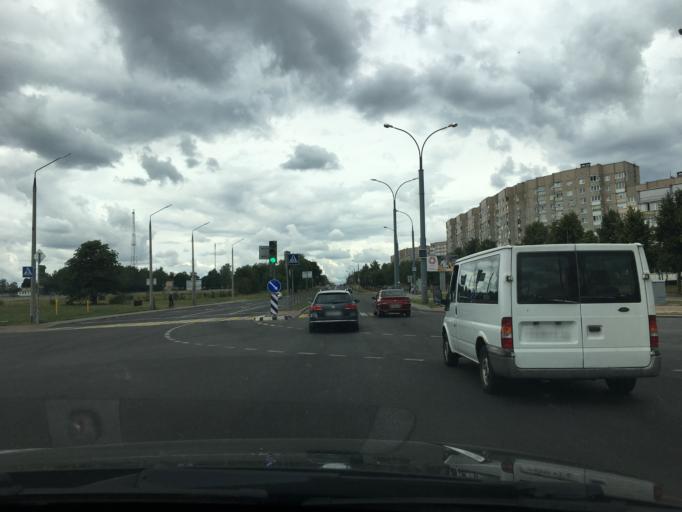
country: BY
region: Grodnenskaya
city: Hrodna
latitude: 53.6408
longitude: 23.8440
